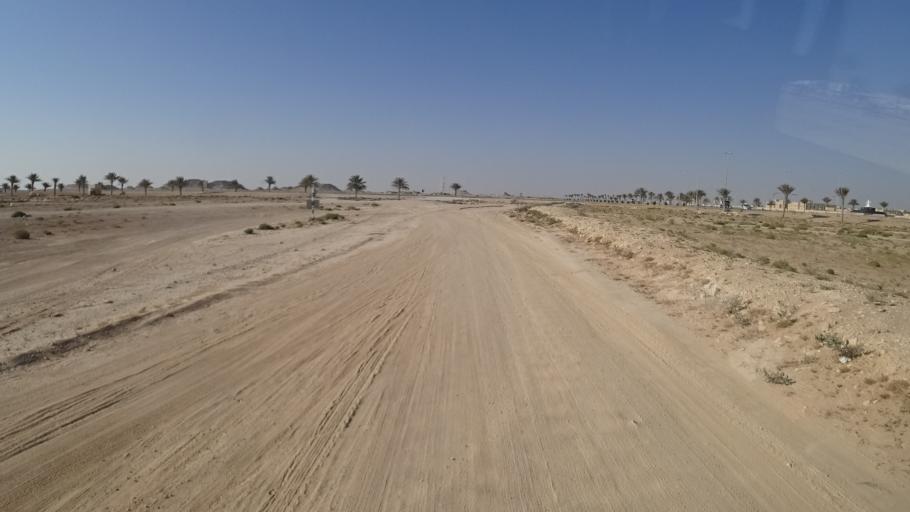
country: OM
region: Zufar
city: Salalah
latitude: 17.6106
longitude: 54.0319
